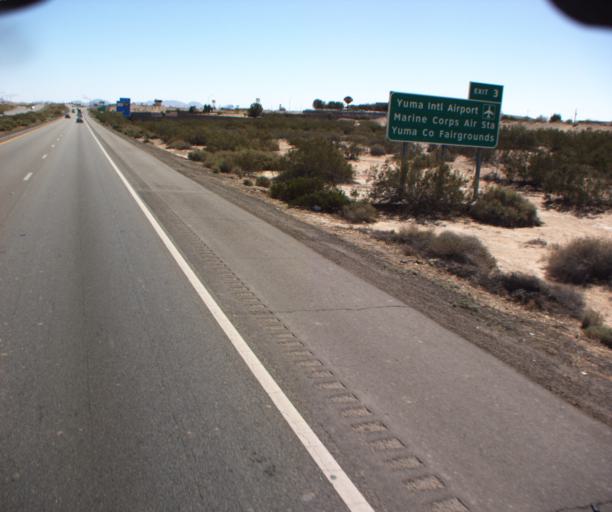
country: US
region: Arizona
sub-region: Yuma County
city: Yuma
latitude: 32.6910
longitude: -114.5930
